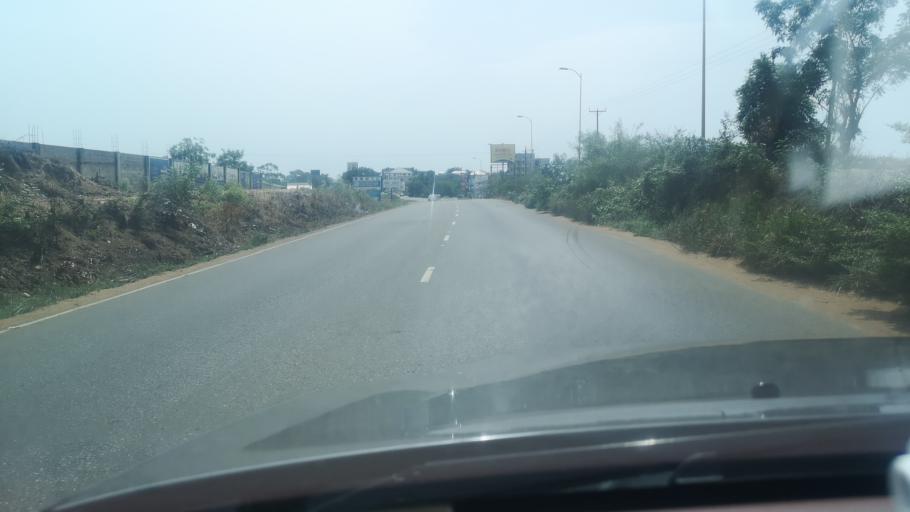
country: GH
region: Greater Accra
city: Nungua
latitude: 5.6159
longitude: -0.0643
